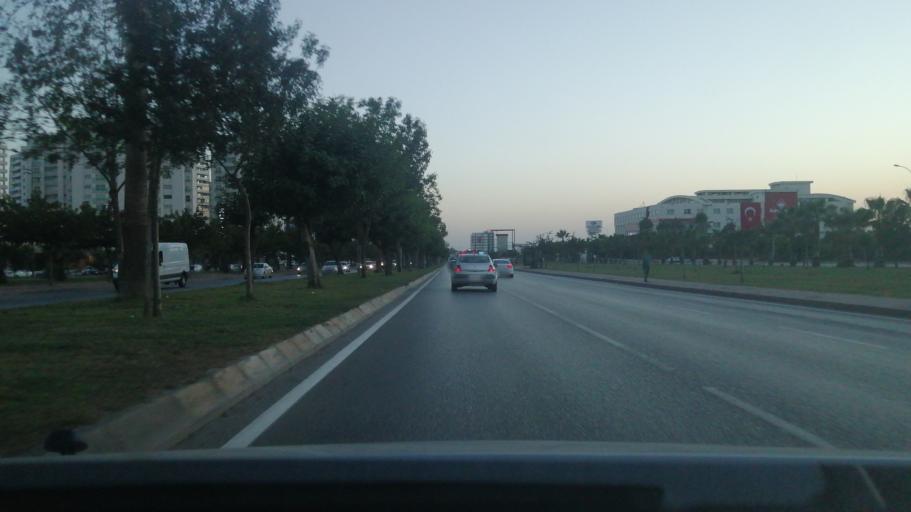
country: TR
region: Adana
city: Seyhan
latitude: 37.0208
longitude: 35.2528
